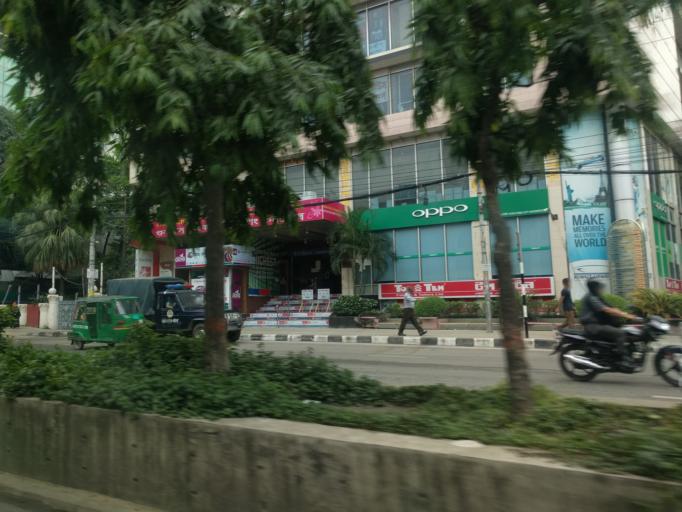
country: BD
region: Dhaka
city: Paltan
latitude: 23.7921
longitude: 90.4154
